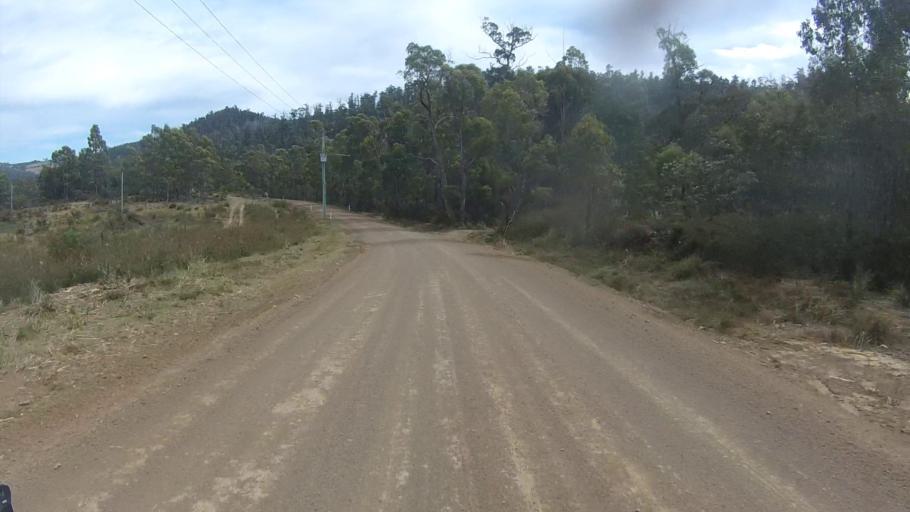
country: AU
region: Tasmania
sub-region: Sorell
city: Sorell
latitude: -42.7548
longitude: 147.7999
